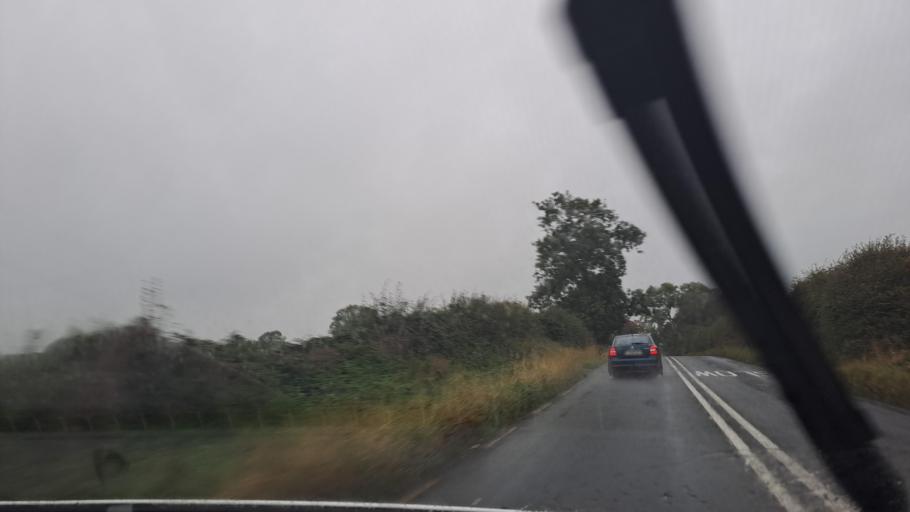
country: IE
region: Leinster
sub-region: Lu
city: Dundalk
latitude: 53.9931
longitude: -6.4553
